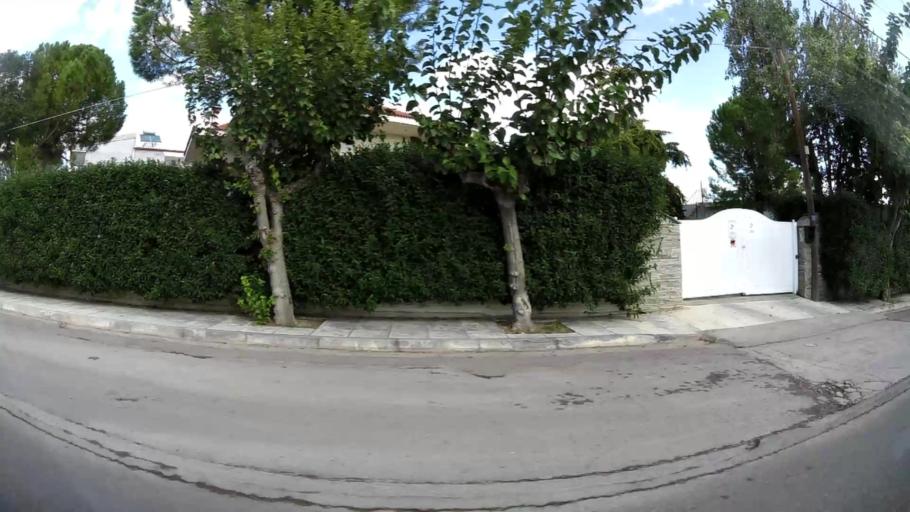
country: GR
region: Attica
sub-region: Nomarchia Anatolikis Attikis
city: Acharnes
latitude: 38.1034
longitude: 23.7399
